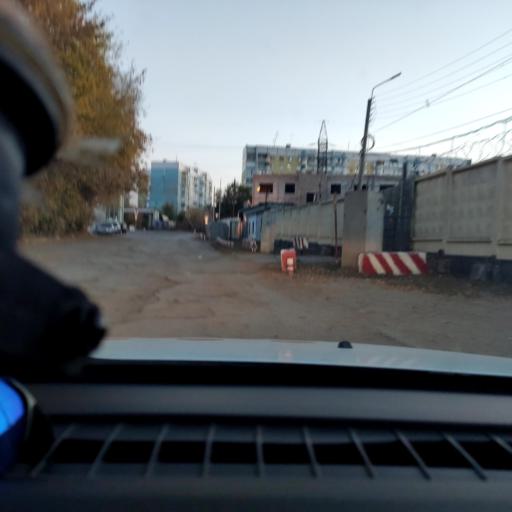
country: RU
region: Samara
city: Samara
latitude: 53.1855
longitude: 50.1395
